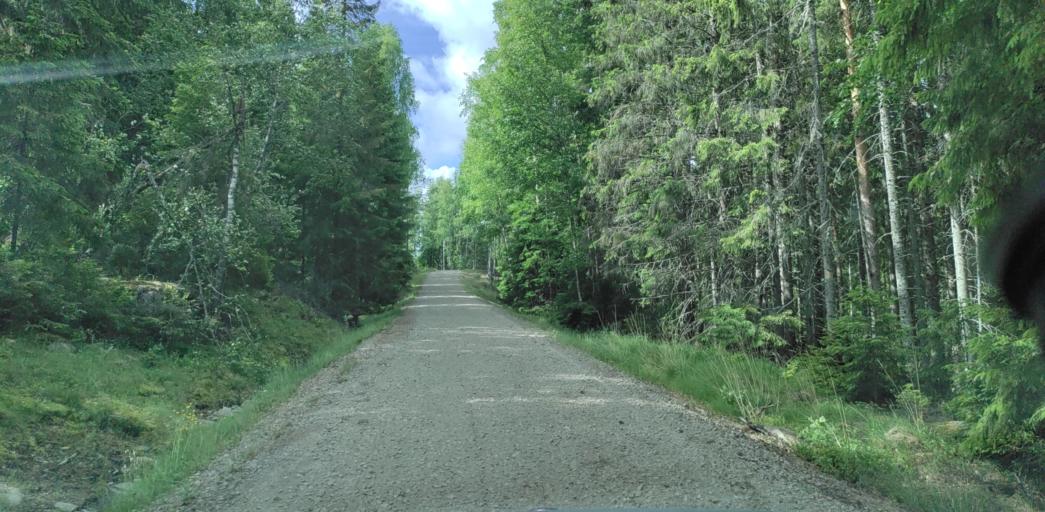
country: SE
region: Vaermland
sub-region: Munkfors Kommun
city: Munkfors
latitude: 59.9682
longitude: 13.4121
